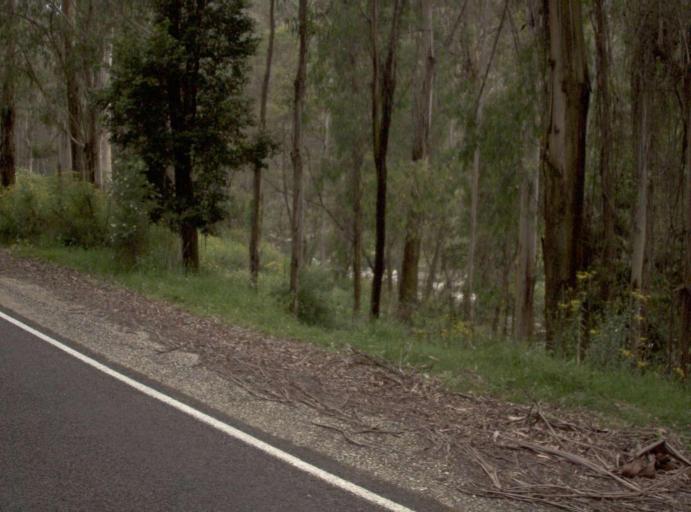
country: AU
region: New South Wales
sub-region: Bombala
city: Bombala
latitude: -37.4246
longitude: 149.2003
